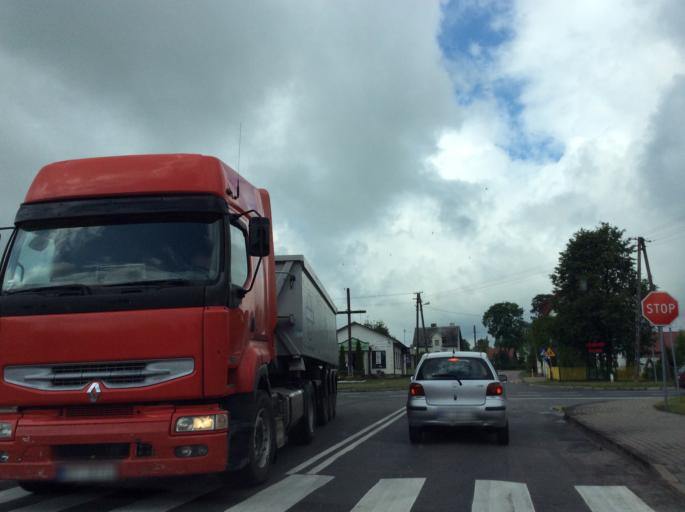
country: PL
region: Warmian-Masurian Voivodeship
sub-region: Powiat szczycienski
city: Rozogi
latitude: 53.4838
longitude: 21.3584
